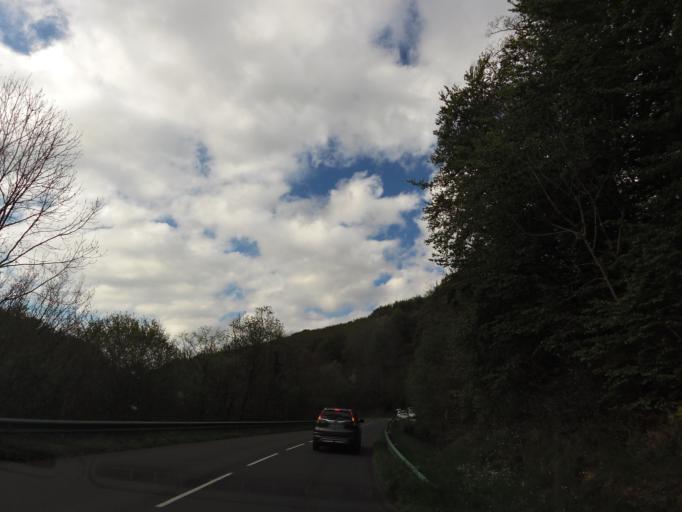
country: FR
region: Midi-Pyrenees
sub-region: Departement du Tarn
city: Soreze
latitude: 43.4176
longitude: 2.0613
